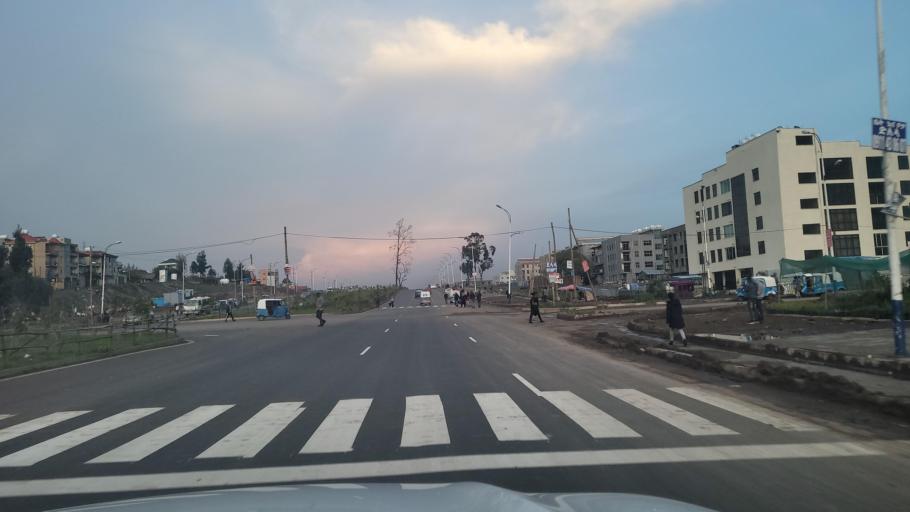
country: ET
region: Adis Abeba
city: Addis Ababa
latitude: 8.9415
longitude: 38.7213
